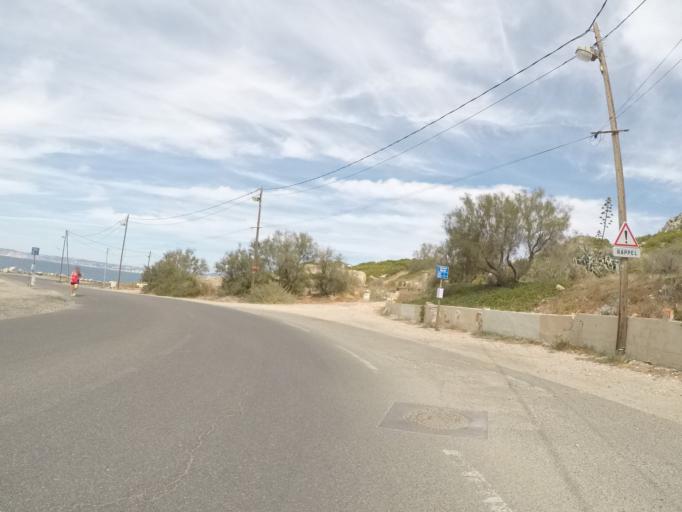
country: FR
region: Provence-Alpes-Cote d'Azur
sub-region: Departement des Bouches-du-Rhone
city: Marseille 08
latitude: 43.2235
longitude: 5.3466
